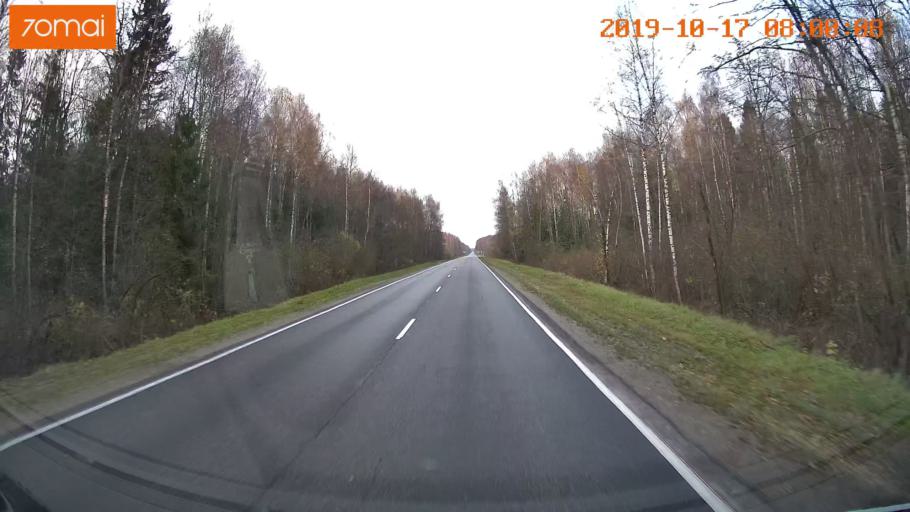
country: RU
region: Vladimir
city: Bavleny
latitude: 56.3863
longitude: 39.5244
